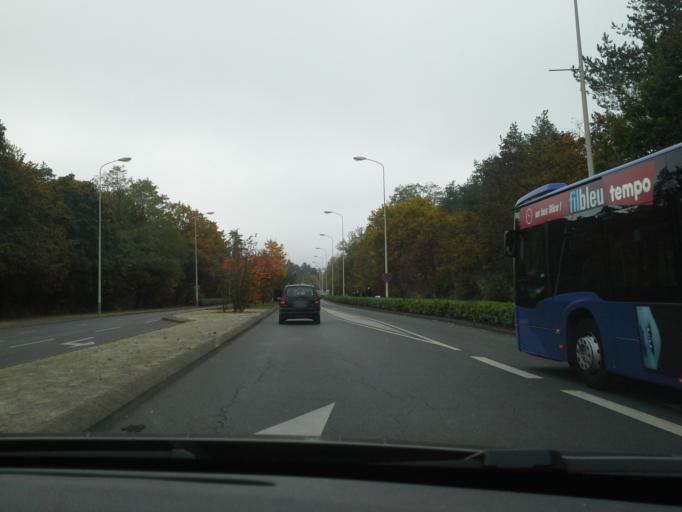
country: FR
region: Centre
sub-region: Departement d'Indre-et-Loire
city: Tours
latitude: 47.4120
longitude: 0.7030
